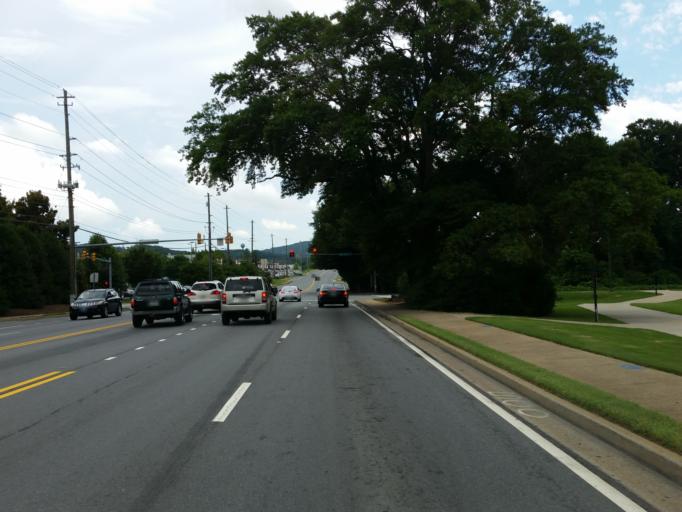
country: US
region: Georgia
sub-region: Cobb County
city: Kennesaw
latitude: 34.0123
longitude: -84.5776
